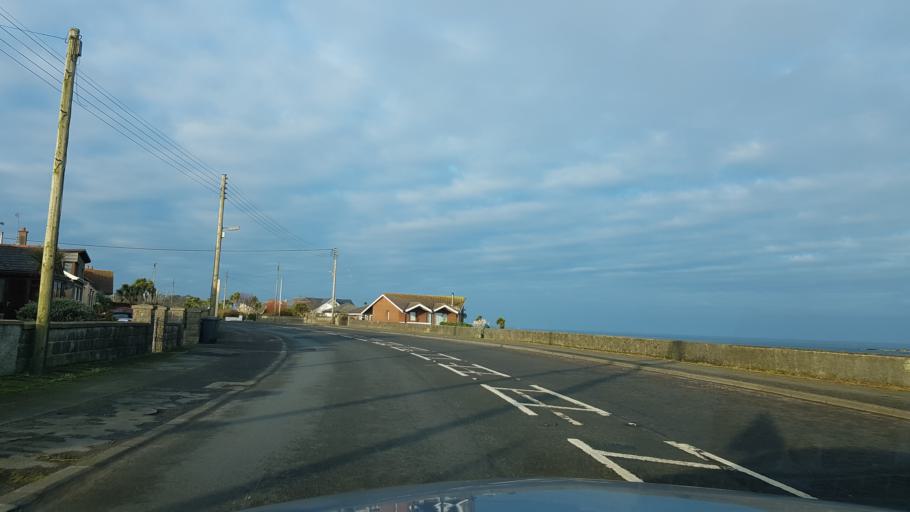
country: GB
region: Northern Ireland
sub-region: Down District
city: Millisle
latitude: 54.6117
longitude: -5.5285
